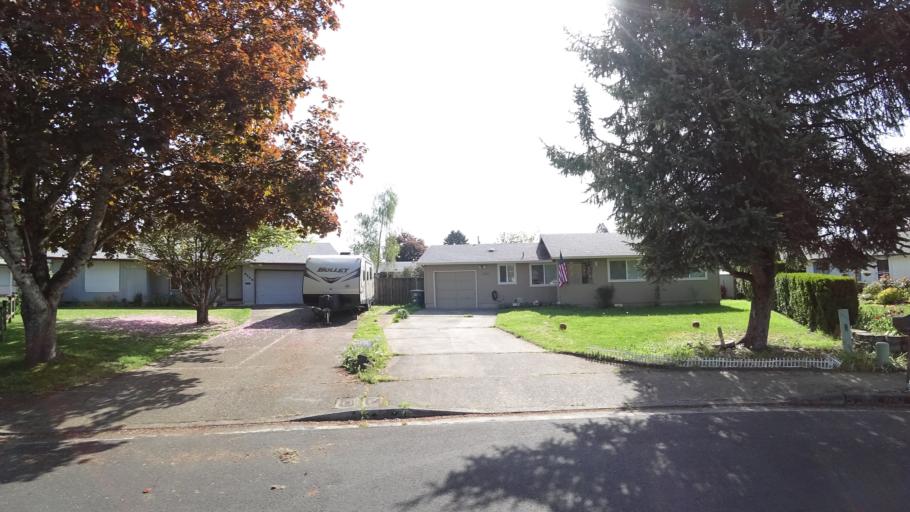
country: US
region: Oregon
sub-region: Washington County
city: Hillsboro
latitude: 45.5233
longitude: -122.9533
